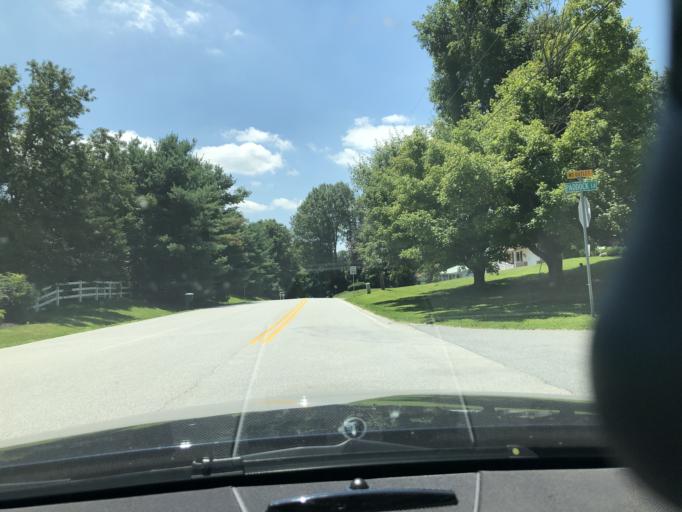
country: US
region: Maryland
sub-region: Carroll County
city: Westminster
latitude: 39.5147
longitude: -76.9235
